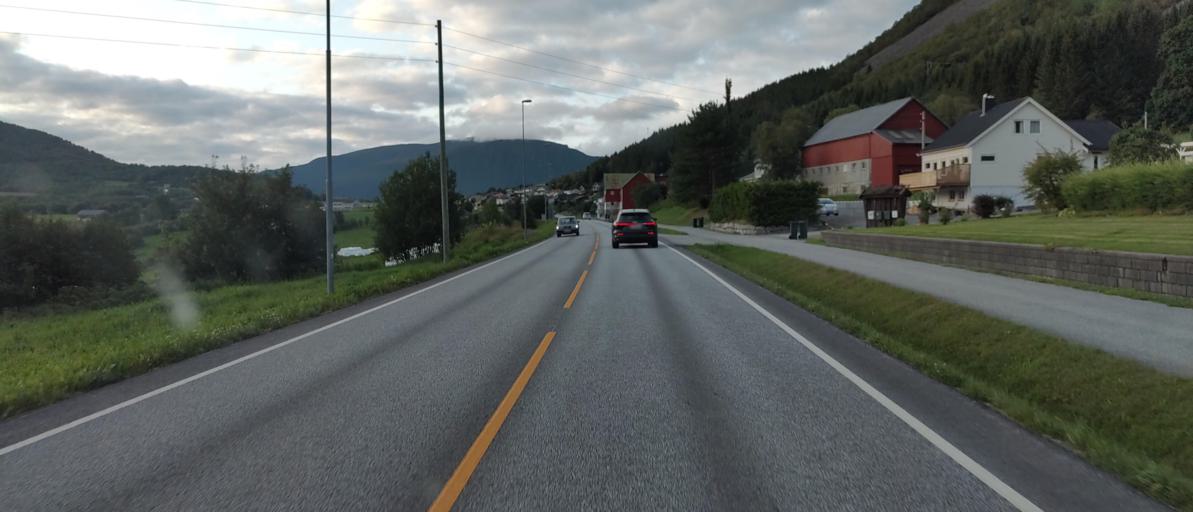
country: NO
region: More og Romsdal
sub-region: Molde
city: Molde
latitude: 62.8074
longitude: 7.2465
